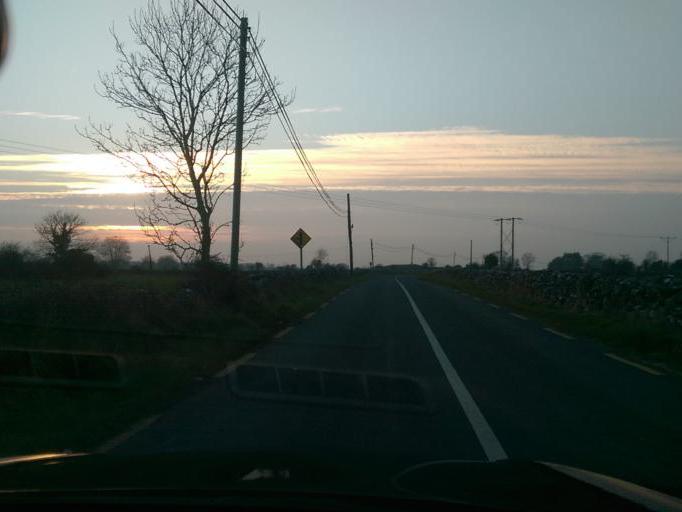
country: IE
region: Connaught
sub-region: County Galway
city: Loughrea
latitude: 53.2149
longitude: -8.6114
